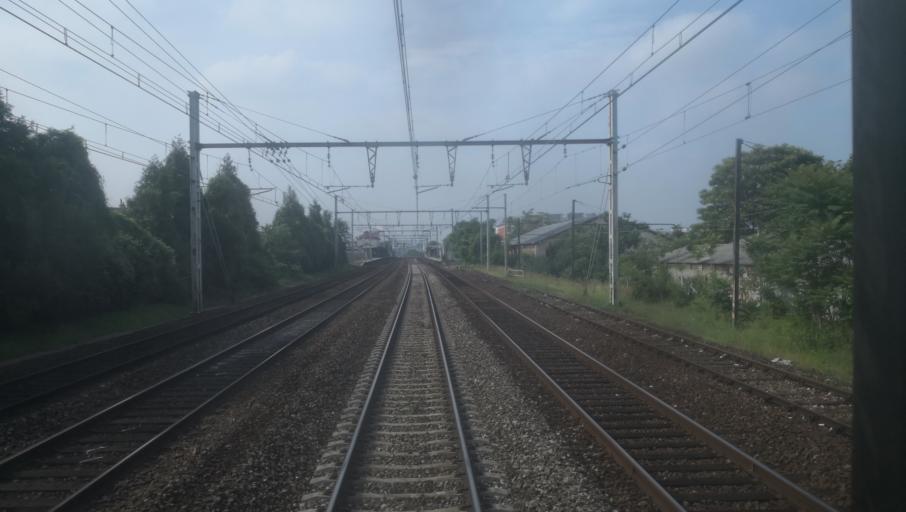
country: FR
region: Ile-de-France
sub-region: Departement du Val-de-Marne
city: Vitry-sur-Seine
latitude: 48.7978
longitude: 2.4042
